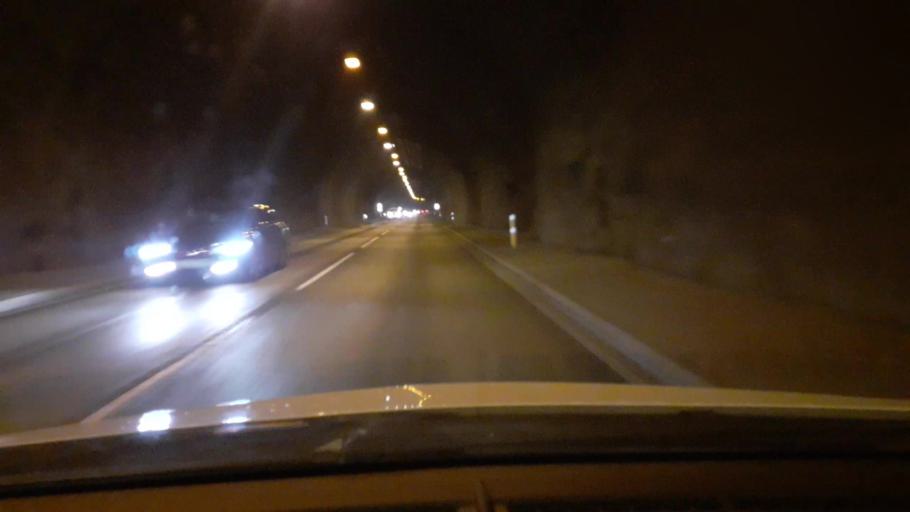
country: IS
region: Capital Region
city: Reykjavik
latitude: 64.2874
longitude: -21.8517
